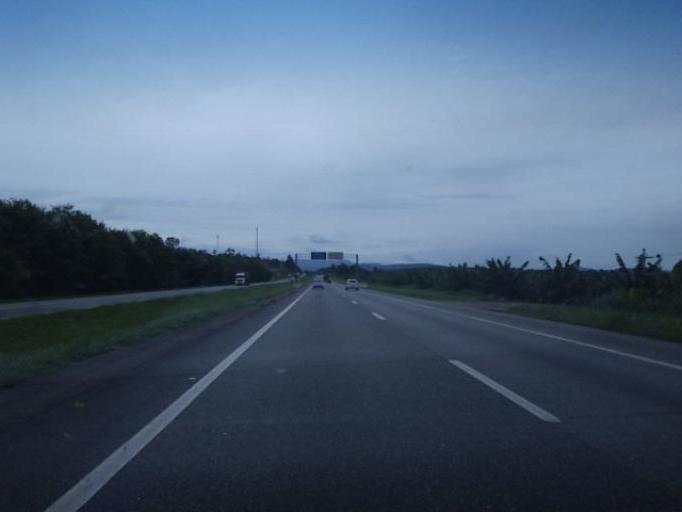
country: BR
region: Sao Paulo
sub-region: Jacupiranga
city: Jacupiranga
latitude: -24.7224
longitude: -48.0571
